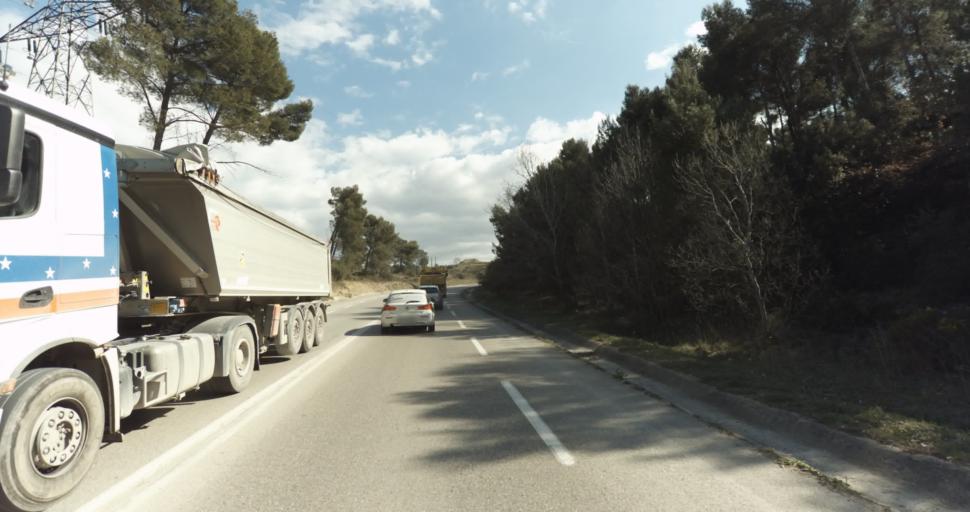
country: FR
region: Provence-Alpes-Cote d'Azur
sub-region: Departement des Bouches-du-Rhone
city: Gardanne
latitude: 43.4580
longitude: 5.4911
